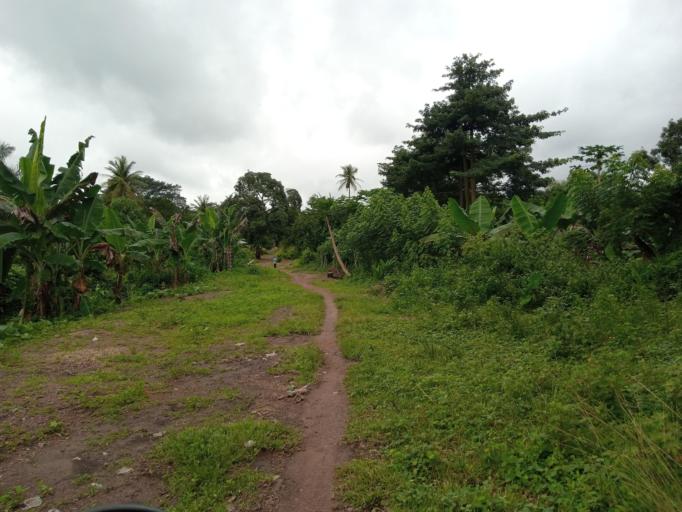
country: SL
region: Southern Province
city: Largo
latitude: 8.2051
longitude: -12.0609
